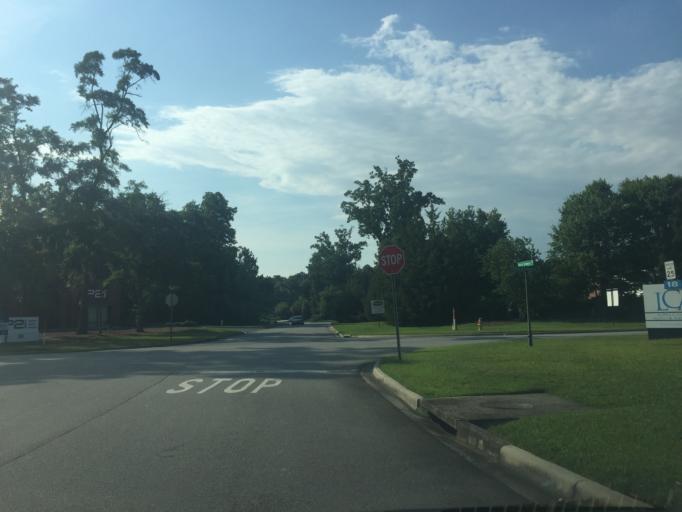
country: US
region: Georgia
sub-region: Chatham County
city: Garden City
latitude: 32.0667
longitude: -81.1625
